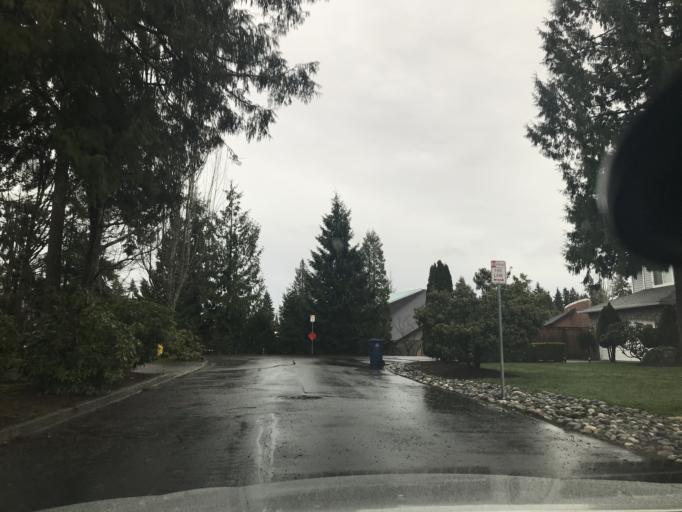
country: US
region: Washington
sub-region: King County
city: Kirkland
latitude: 47.6703
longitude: -122.1822
